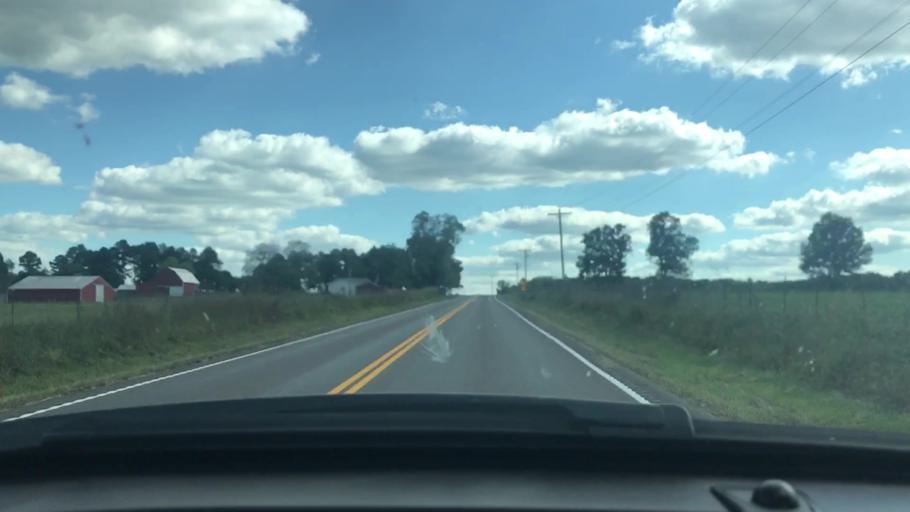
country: US
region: Missouri
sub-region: Wright County
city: Mountain Grove
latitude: 37.2377
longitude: -92.3006
